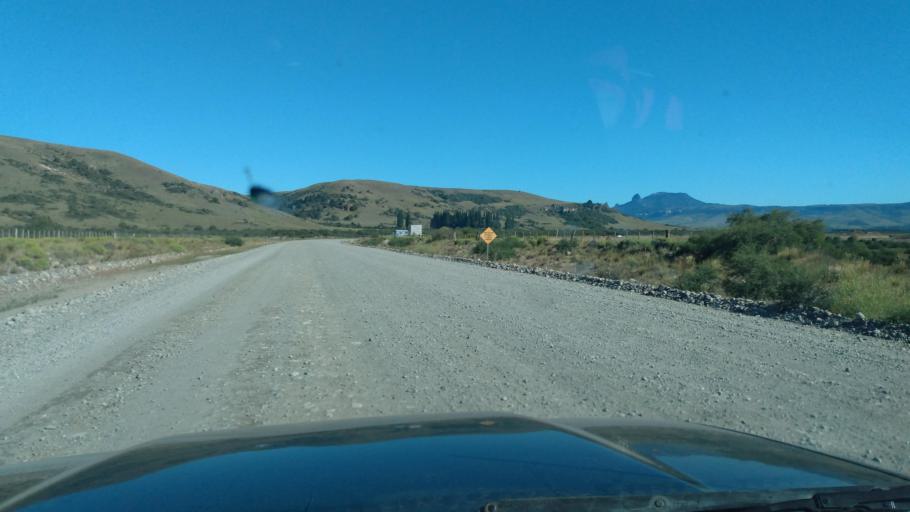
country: AR
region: Neuquen
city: Junin de los Andes
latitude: -39.8589
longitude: -71.1866
